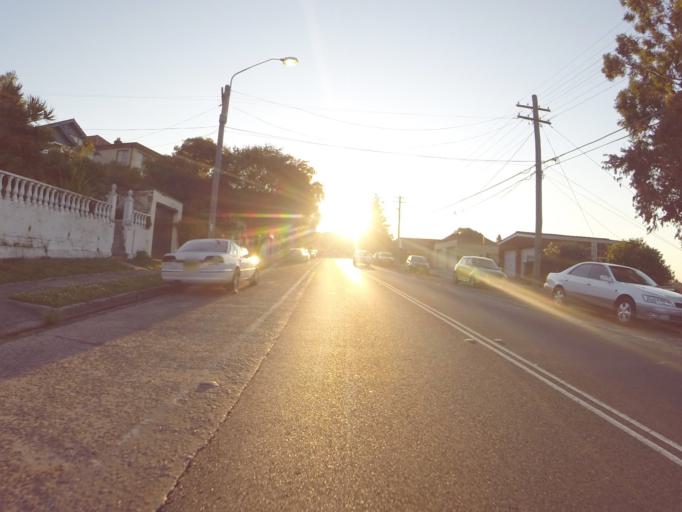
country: AU
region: New South Wales
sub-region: Rockdale
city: Bardwell Valley
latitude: -33.9233
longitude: 151.1386
